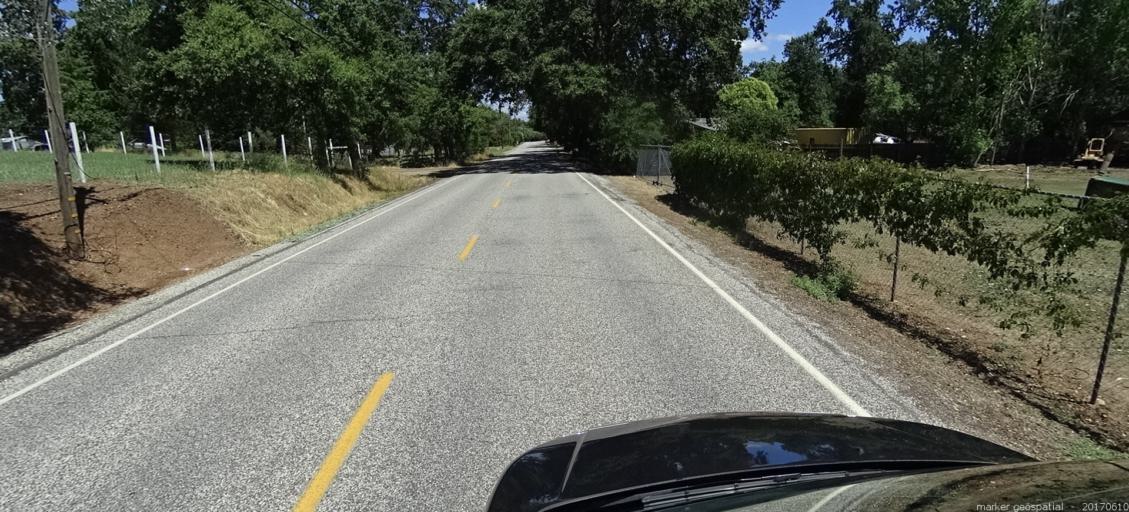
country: US
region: California
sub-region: Butte County
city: Oroville East
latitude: 39.4722
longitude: -121.4590
